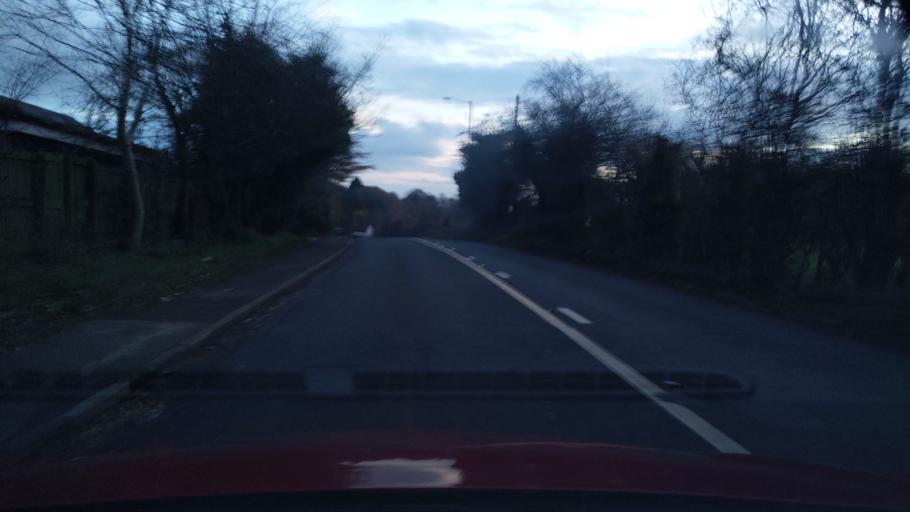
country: GB
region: England
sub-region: Lancashire
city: Clayton-le-Woods
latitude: 53.6948
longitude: -2.6735
